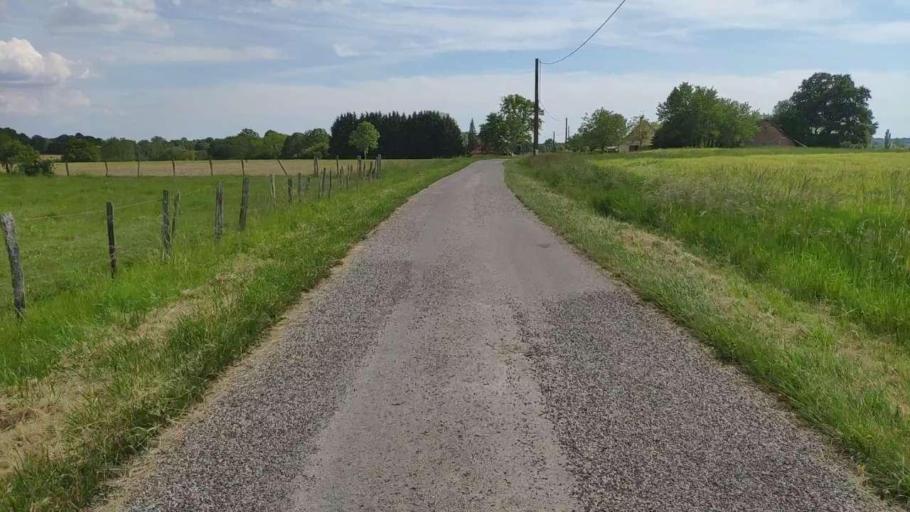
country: FR
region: Franche-Comte
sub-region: Departement du Jura
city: Bletterans
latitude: 46.8128
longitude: 5.3860
